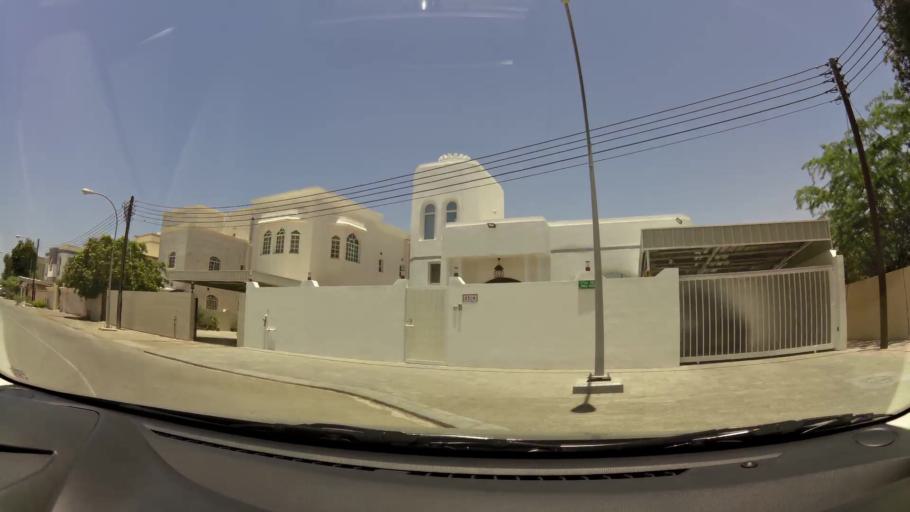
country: OM
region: Muhafazat Masqat
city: Bawshar
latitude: 23.5972
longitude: 58.3959
